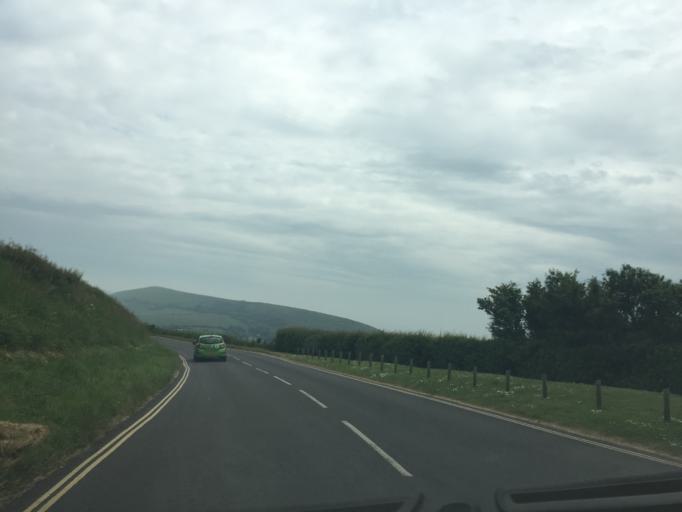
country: GB
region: England
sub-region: Dorset
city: Wool
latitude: 50.6290
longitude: -2.2668
